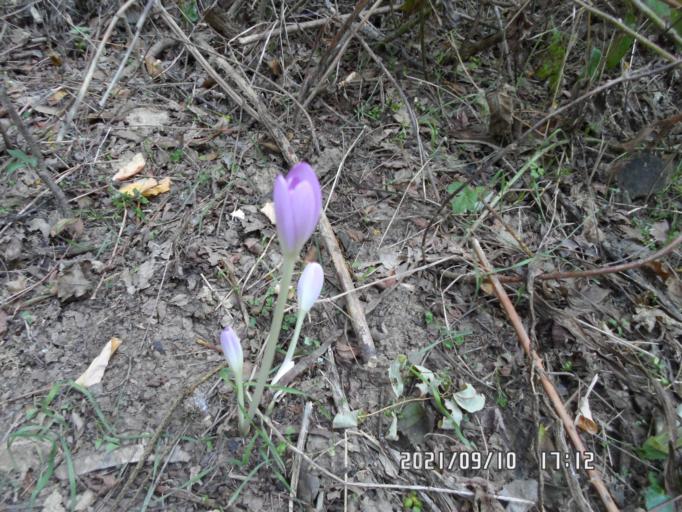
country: HU
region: Zala
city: Nagykanizsa
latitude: 46.5689
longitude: 17.0472
